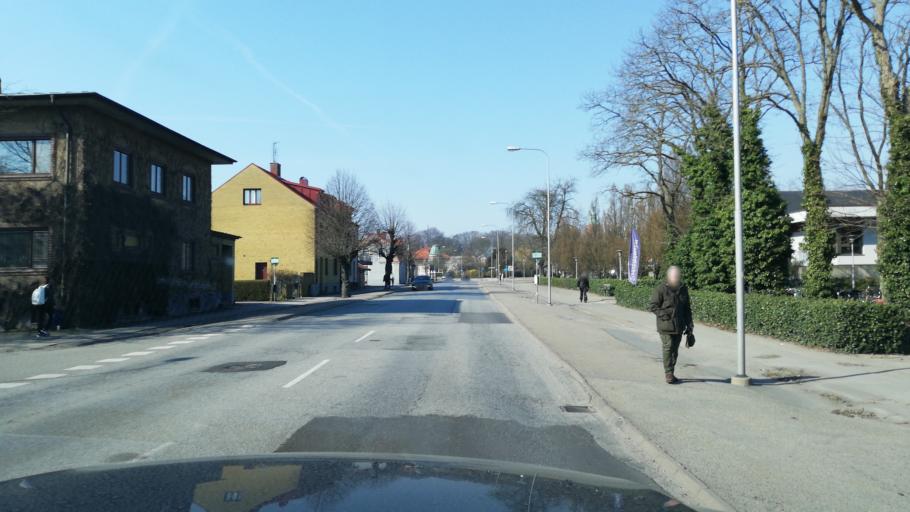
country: SE
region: Skane
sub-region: Ystads Kommun
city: Ystad
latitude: 55.4329
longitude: 13.8279
